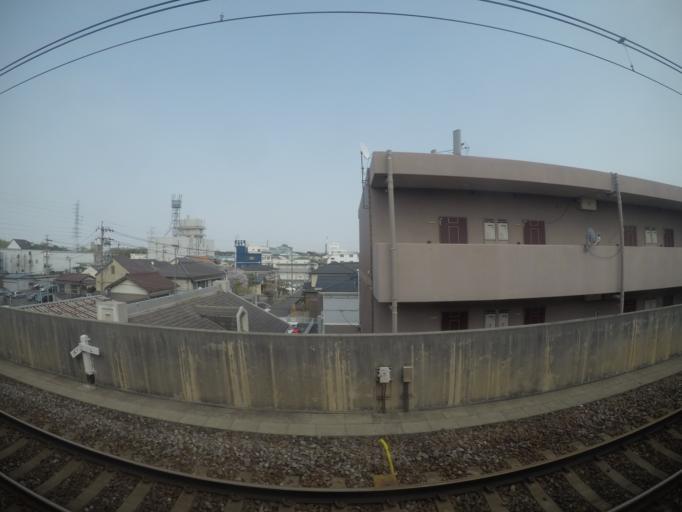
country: JP
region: Aichi
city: Obu
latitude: 35.0811
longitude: 136.9096
